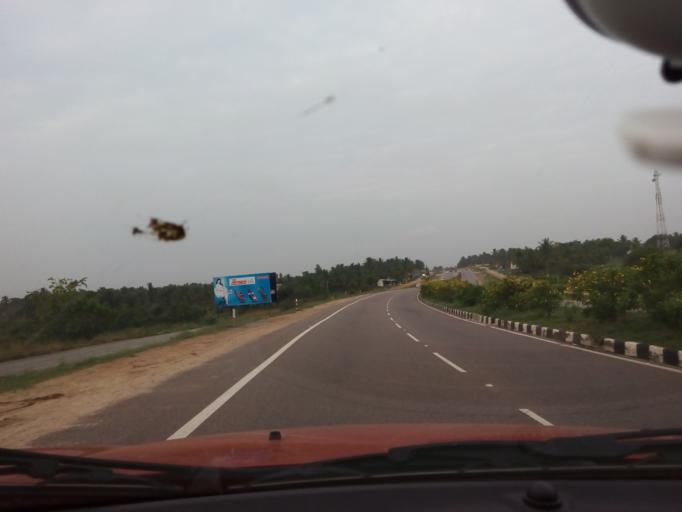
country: IN
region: Karnataka
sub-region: Tumkur
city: Kunigal
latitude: 12.9989
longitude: 76.9419
